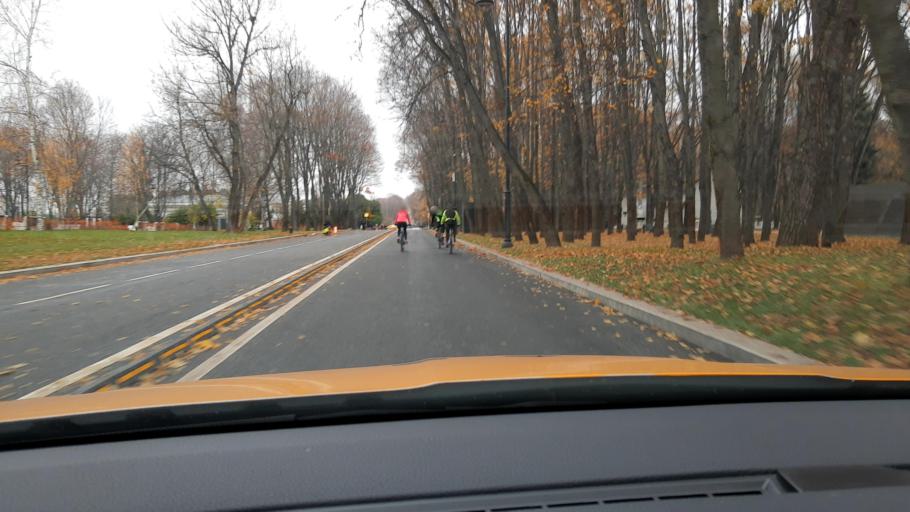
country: RU
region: Moskovskaya
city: Levoberezhnyy
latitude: 55.8486
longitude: 37.4699
